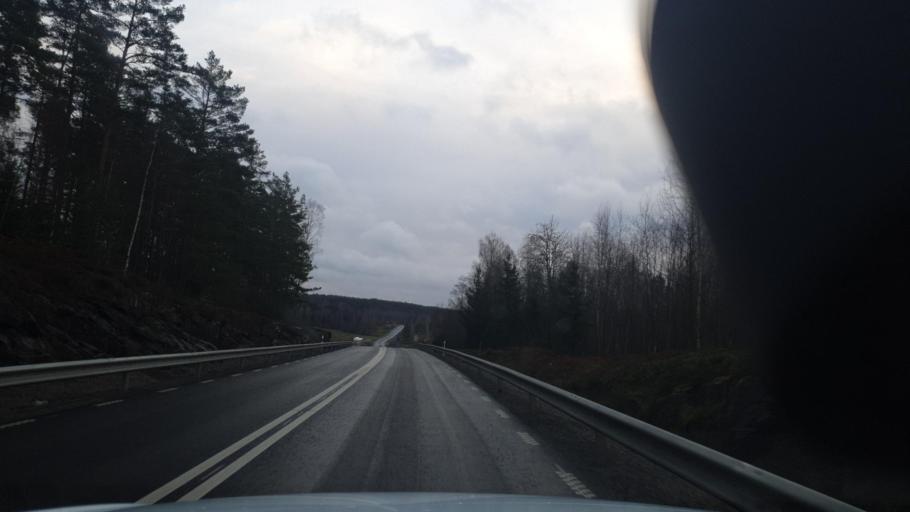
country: SE
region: Vaermland
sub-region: Arvika Kommun
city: Arvika
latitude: 59.7096
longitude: 12.5468
